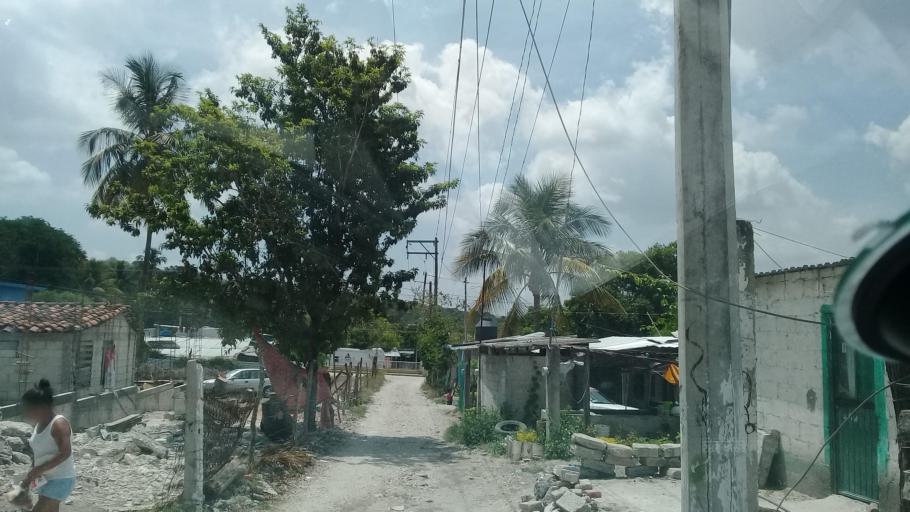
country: MX
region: Veracruz
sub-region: Emiliano Zapata
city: Plan del Rio
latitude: 19.4044
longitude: -96.6534
